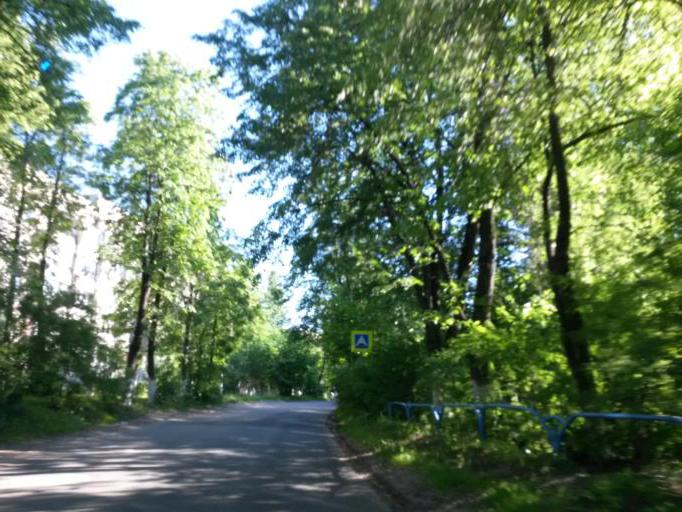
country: RU
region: Moskovskaya
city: Lyubuchany
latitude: 55.2432
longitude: 37.5439
